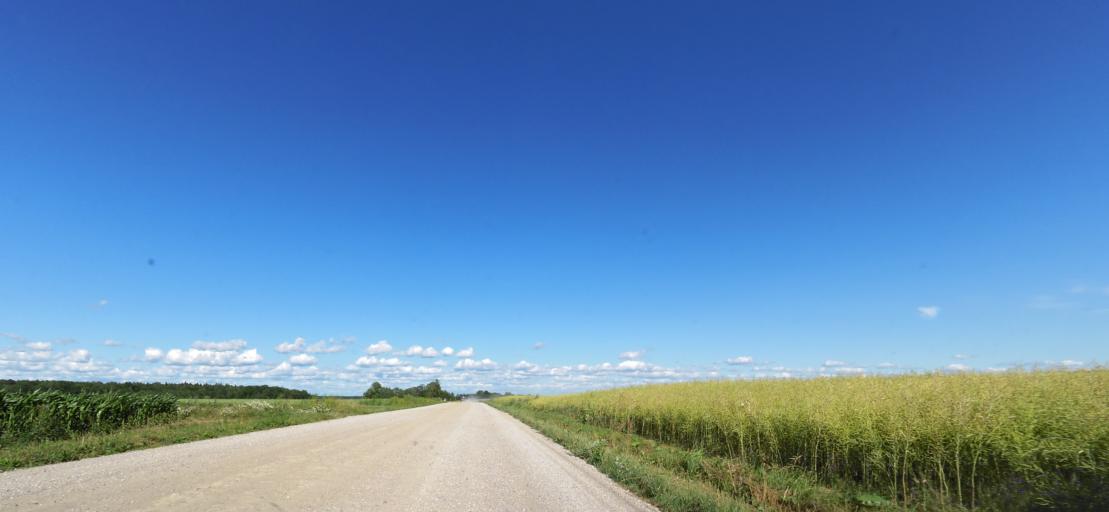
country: LT
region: Panevezys
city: Pasvalys
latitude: 56.1453
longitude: 24.4257
